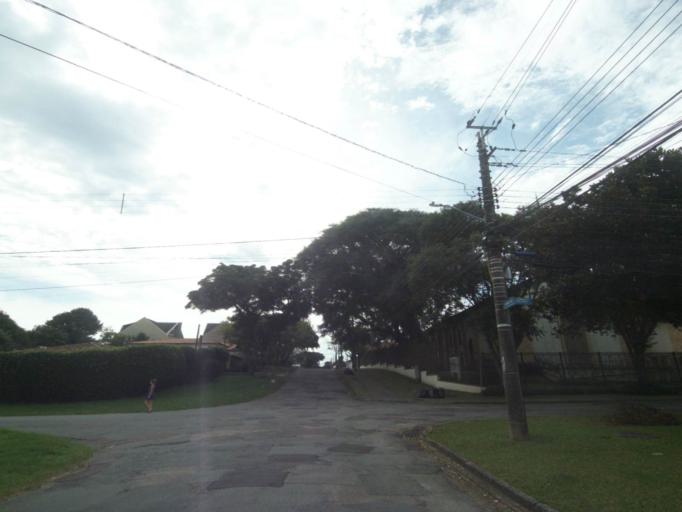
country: BR
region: Parana
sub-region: Pinhais
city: Pinhais
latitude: -25.4444
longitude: -49.2192
